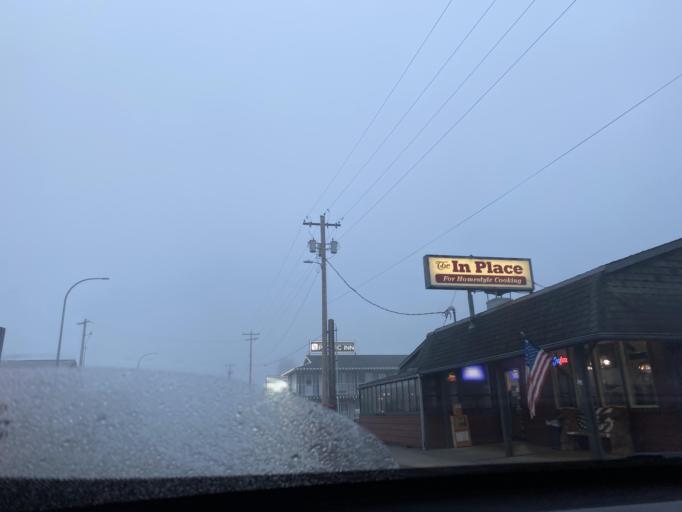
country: US
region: Washington
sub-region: Clallam County
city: Forks
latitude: 47.9480
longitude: -124.3855
